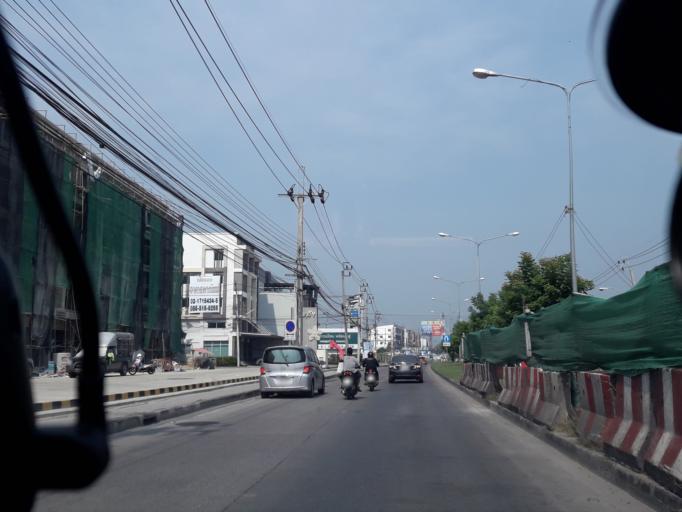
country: TH
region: Bangkok
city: Khlong Sam Wa
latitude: 13.8340
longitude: 100.7200
